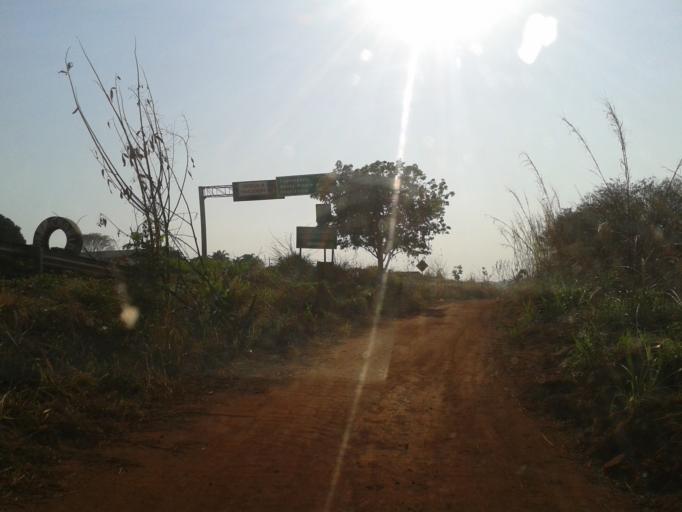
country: BR
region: Minas Gerais
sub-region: Ituiutaba
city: Ituiutaba
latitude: -18.9649
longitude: -49.4810
